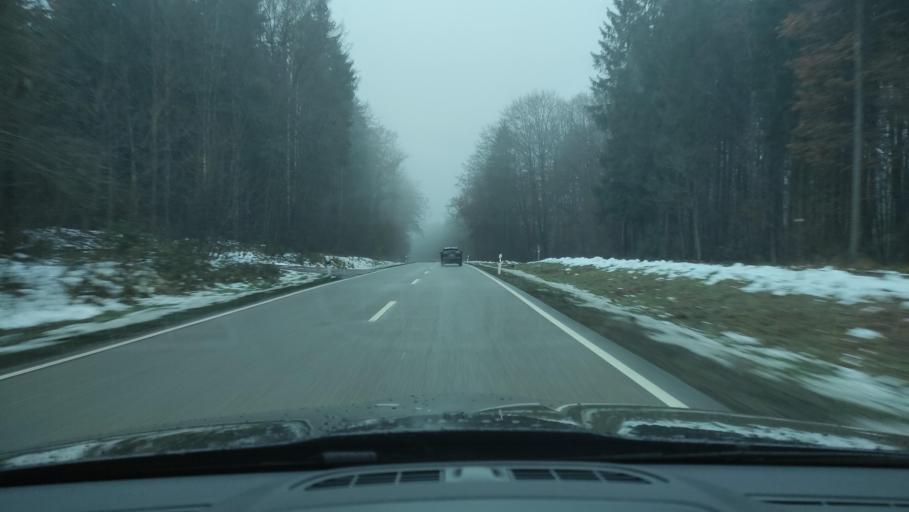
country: DE
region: Bavaria
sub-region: Swabia
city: Weissenhorn
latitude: 48.2910
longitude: 10.1884
